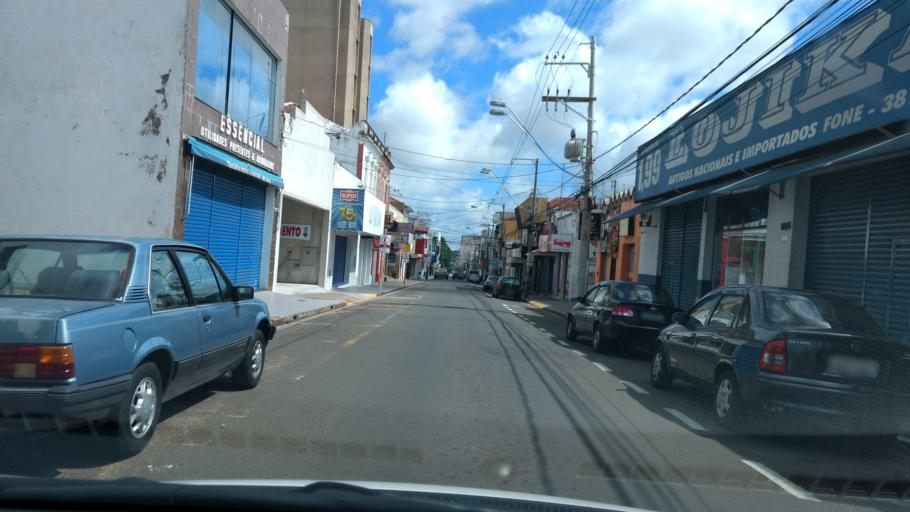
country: BR
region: Sao Paulo
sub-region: Botucatu
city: Botucatu
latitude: -22.8911
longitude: -48.4410
